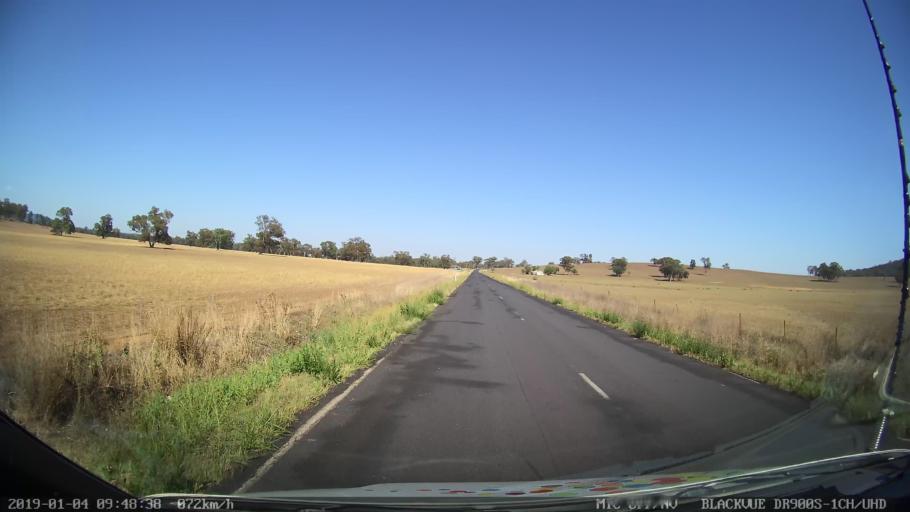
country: AU
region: New South Wales
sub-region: Cabonne
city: Canowindra
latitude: -33.5971
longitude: 148.4306
